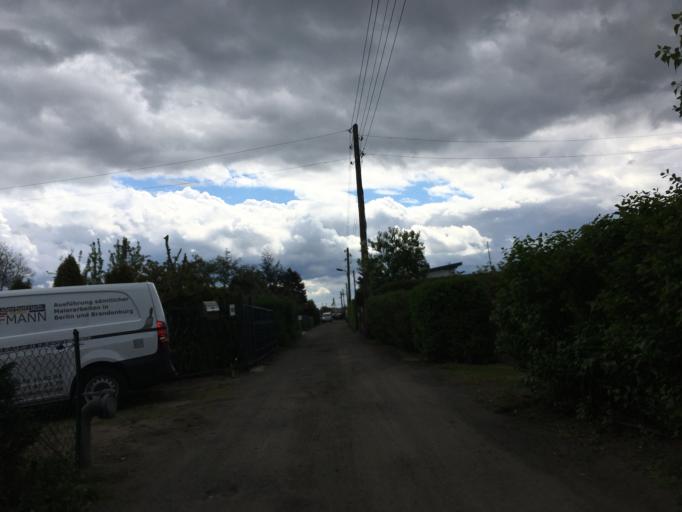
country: DE
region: Berlin
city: Buchholz
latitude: 52.6197
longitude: 13.4163
